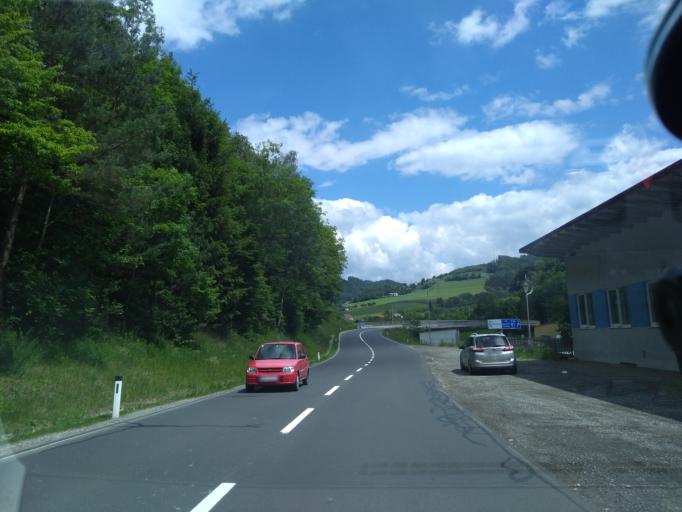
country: AT
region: Styria
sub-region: Politischer Bezirk Bruck-Muerzzuschlag
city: Bruck an der Mur
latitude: 47.4018
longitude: 15.2840
